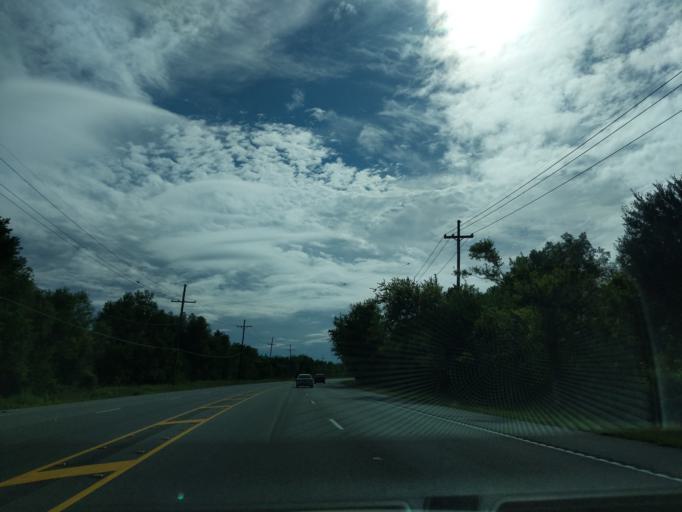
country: US
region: Louisiana
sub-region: Saint Bernard Parish
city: Meraux
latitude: 30.0621
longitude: -89.8665
